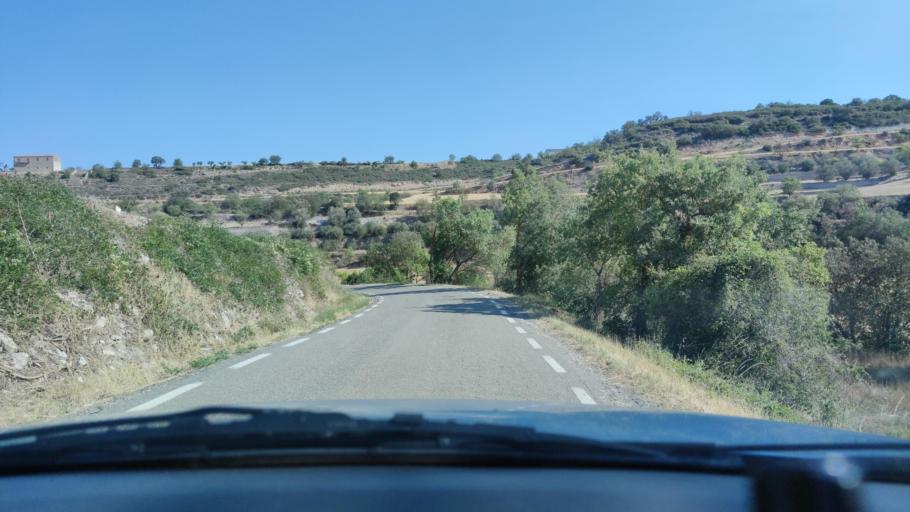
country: ES
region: Catalonia
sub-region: Provincia de Lleida
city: Ivorra
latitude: 41.7358
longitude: 1.3553
